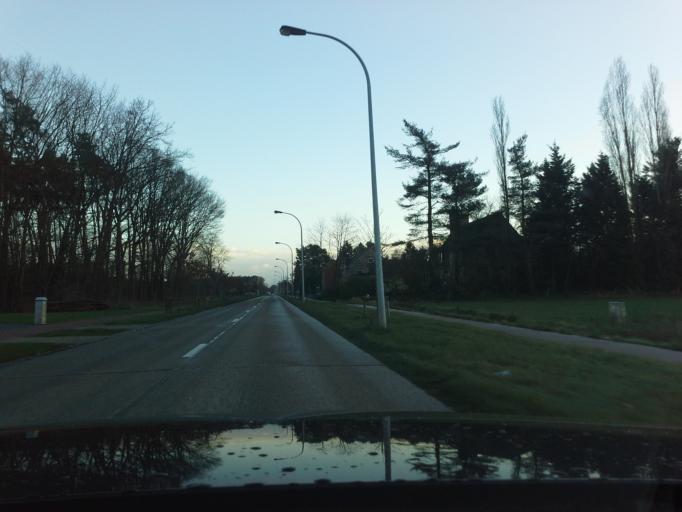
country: BE
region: Flanders
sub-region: Provincie Antwerpen
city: Geel
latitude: 51.1608
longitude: 5.0378
